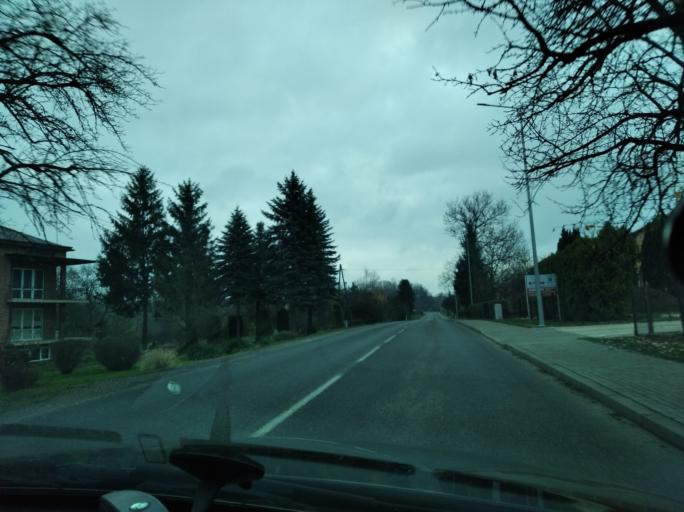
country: PL
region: Subcarpathian Voivodeship
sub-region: Powiat przeworski
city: Sietesz
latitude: 50.0028
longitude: 22.3493
